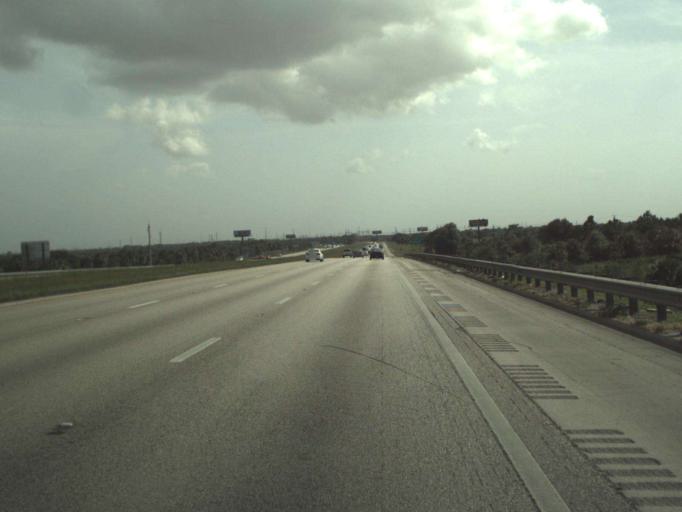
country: US
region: Florida
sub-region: Saint Lucie County
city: Fort Pierce South
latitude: 27.3949
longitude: -80.3954
